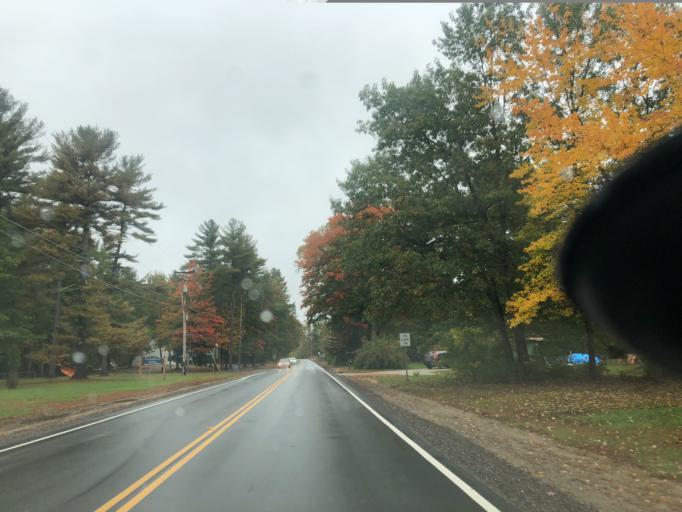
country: US
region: New Hampshire
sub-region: Strafford County
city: Lee
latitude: 43.1260
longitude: -71.0066
